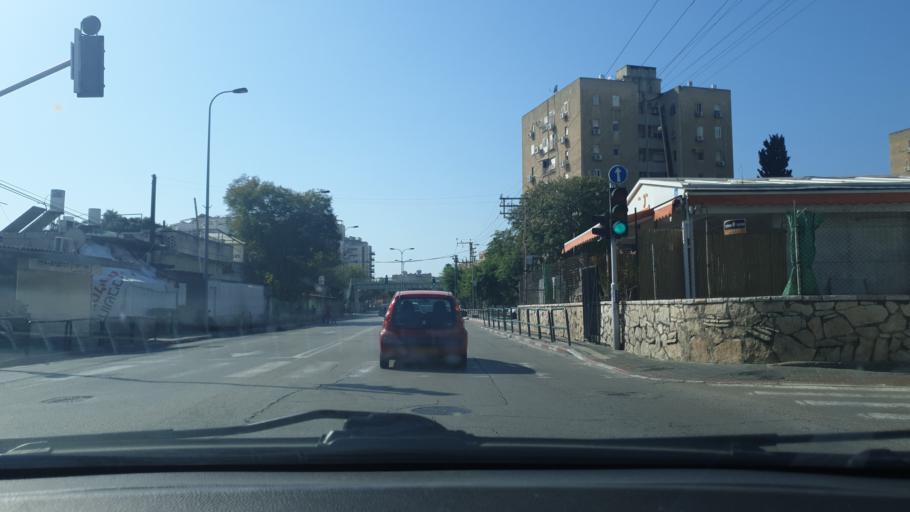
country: IL
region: Tel Aviv
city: Azor
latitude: 32.0449
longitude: 34.8111
